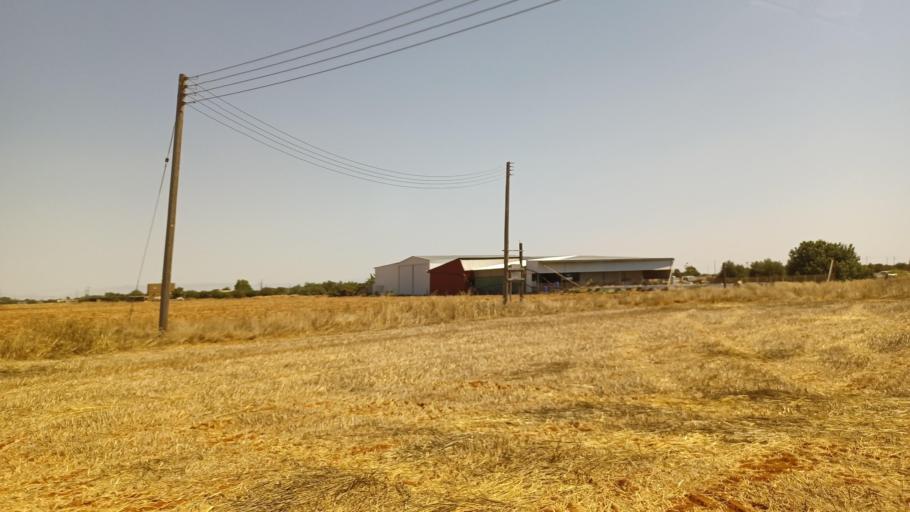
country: CY
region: Ammochostos
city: Avgorou
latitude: 35.0281
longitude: 33.8087
